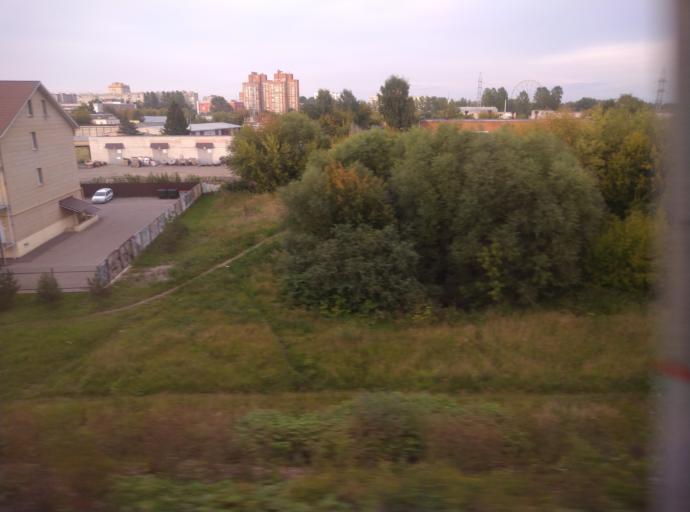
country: RU
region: Jaroslavl
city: Yaroslavl
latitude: 57.6161
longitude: 39.8488
